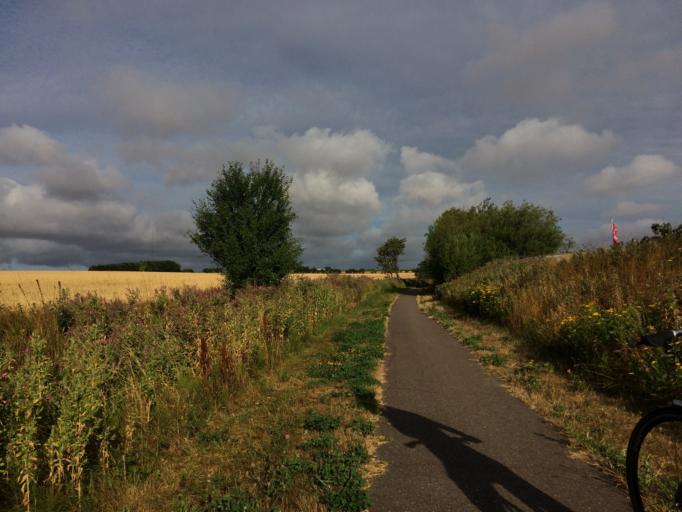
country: DK
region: Central Jutland
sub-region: Skive Kommune
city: Skive
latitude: 56.5898
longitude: 9.0153
